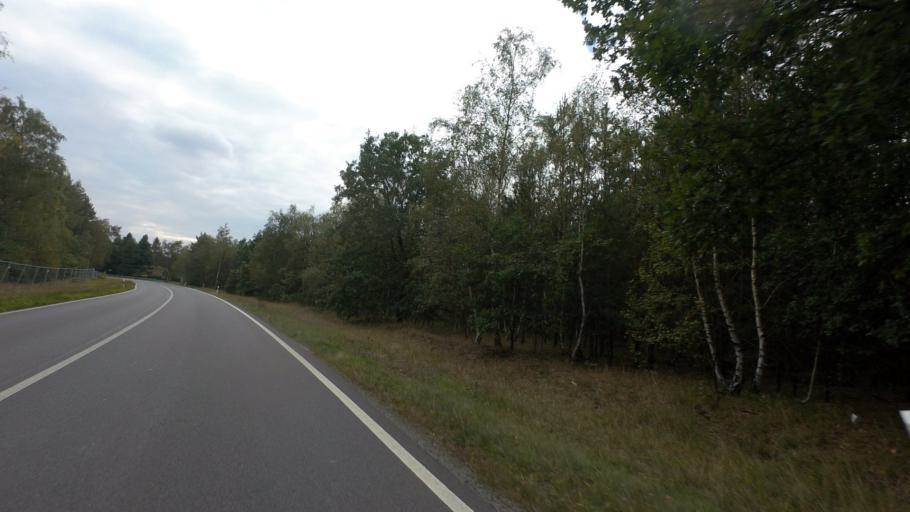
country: DE
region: Saxony
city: Wittichenau
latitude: 51.3749
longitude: 14.2891
